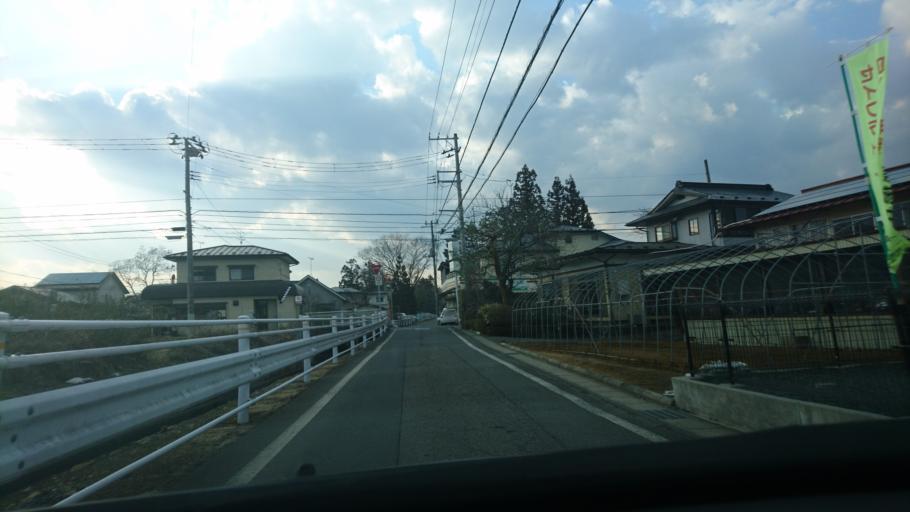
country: JP
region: Iwate
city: Ichinoseki
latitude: 38.9377
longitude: 141.0927
